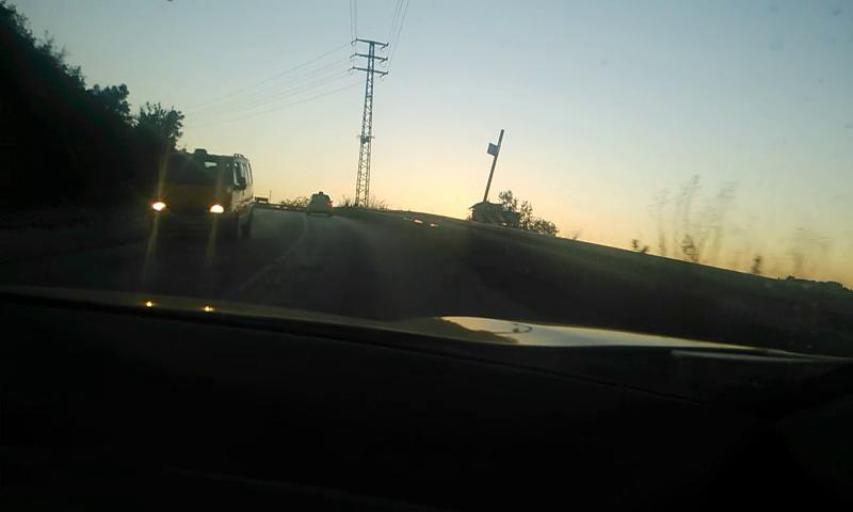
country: PS
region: West Bank
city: Jifna
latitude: 31.9572
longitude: 35.2188
